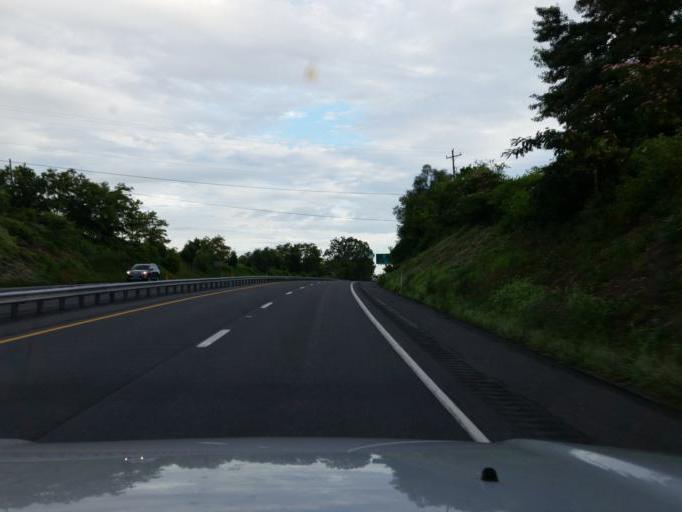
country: US
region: Pennsylvania
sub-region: Adams County
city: Lake Meade
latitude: 40.0060
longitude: -77.1027
